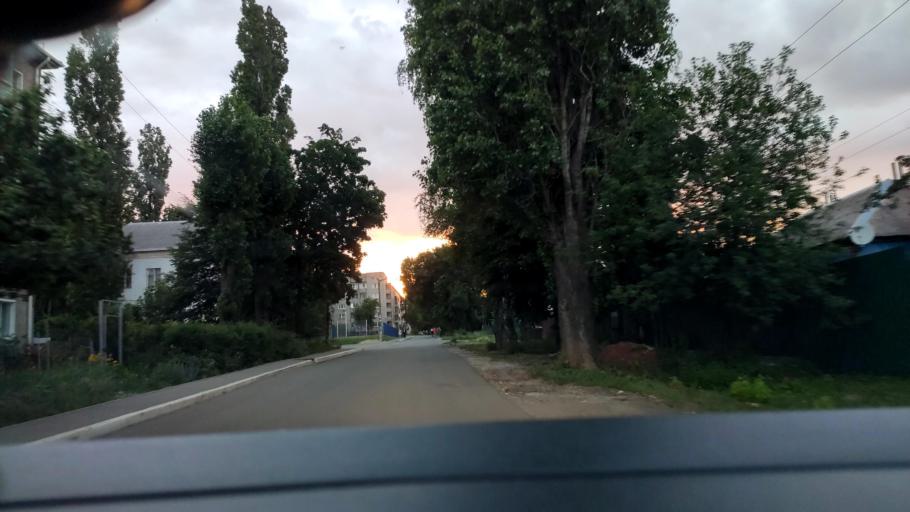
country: RU
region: Voronezj
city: Semiluki
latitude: 51.6939
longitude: 39.0260
